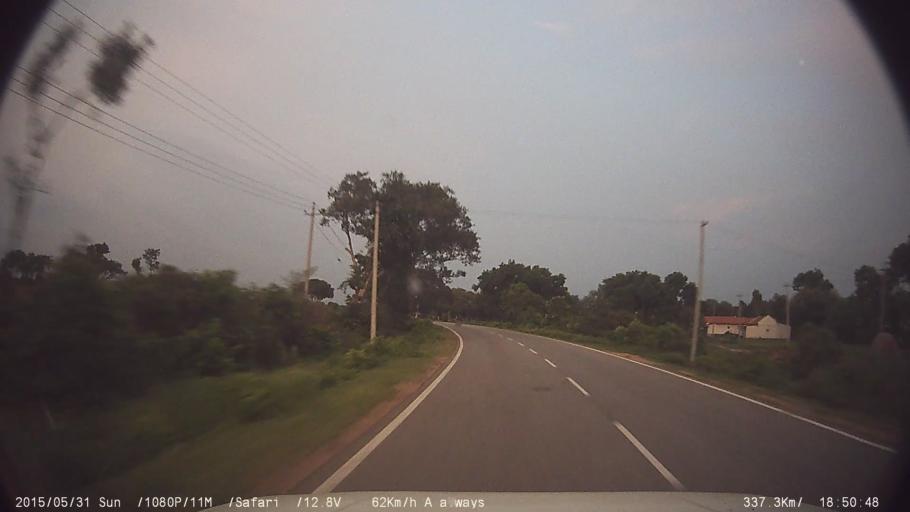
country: IN
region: Karnataka
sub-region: Mysore
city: Tirumakudal Narsipur
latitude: 12.1800
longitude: 76.8616
